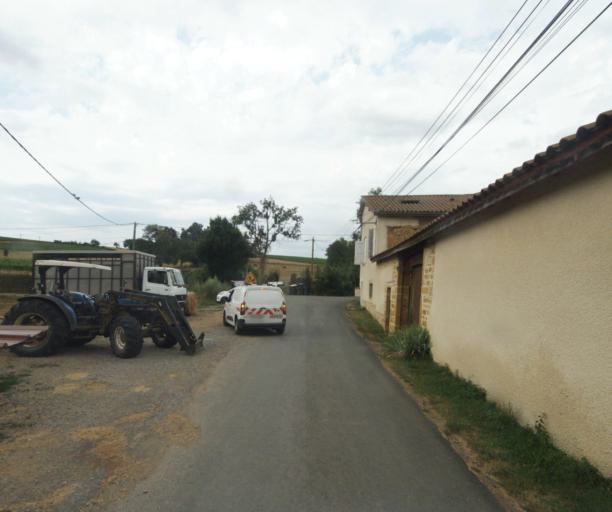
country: FR
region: Rhone-Alpes
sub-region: Departement du Rhone
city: Bully
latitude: 45.8718
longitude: 4.5755
